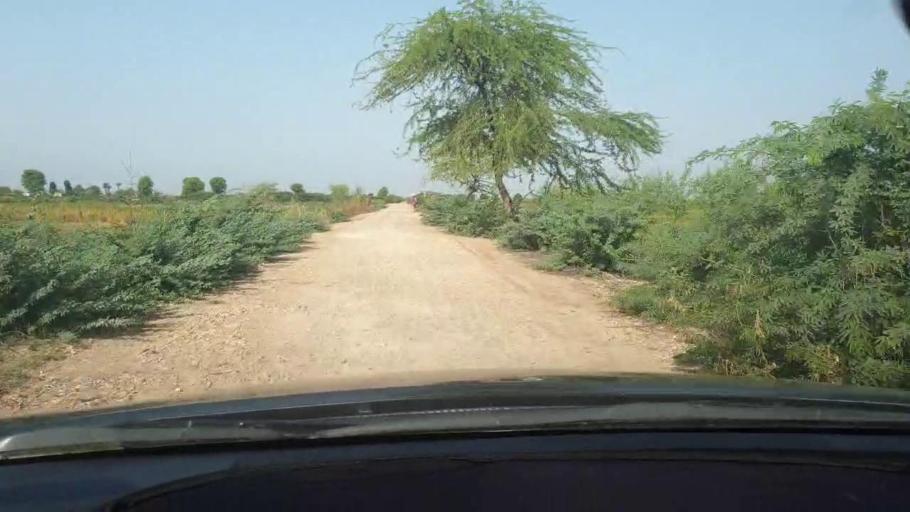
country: PK
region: Sindh
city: Tando Bago
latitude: 24.6800
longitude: 69.1379
